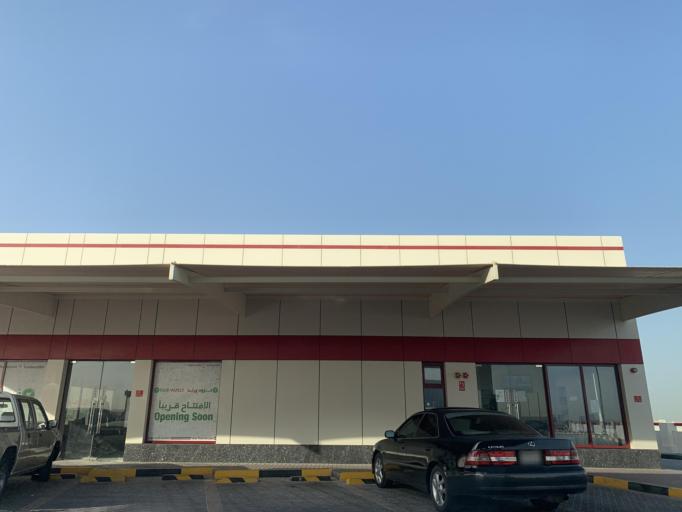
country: BH
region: Muharraq
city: Al Muharraq
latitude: 26.2816
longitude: 50.5967
